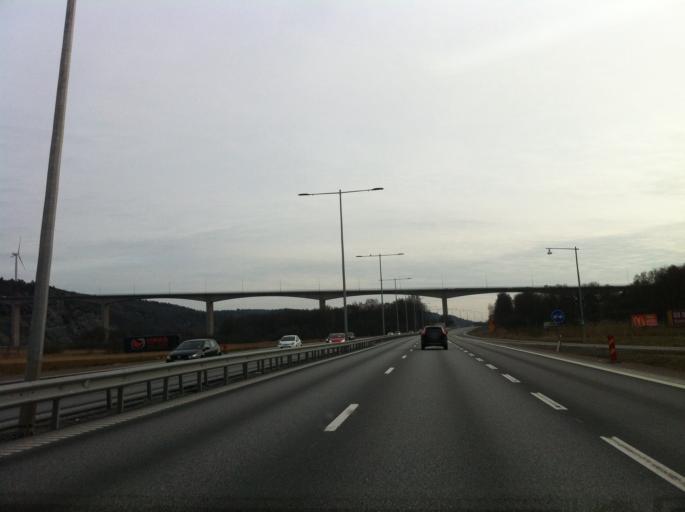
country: SE
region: Vaestra Goetaland
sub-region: Kungalvs Kommun
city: Kungalv
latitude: 57.8634
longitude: 11.9749
